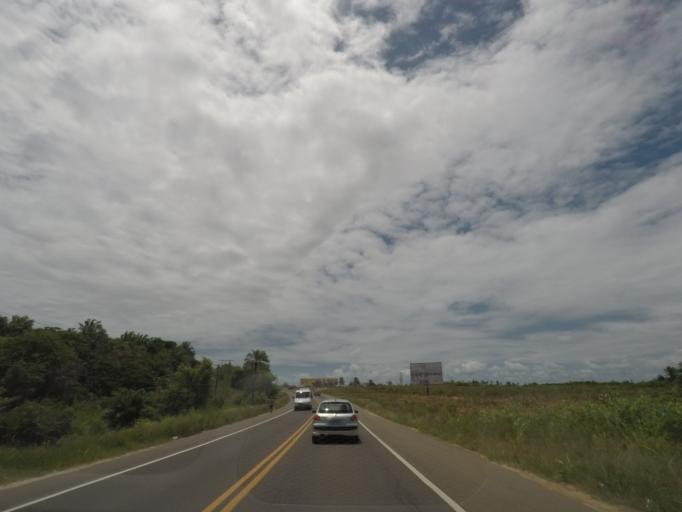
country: BR
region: Bahia
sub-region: Itaparica
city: Itaparica
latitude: -12.9407
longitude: -38.6302
